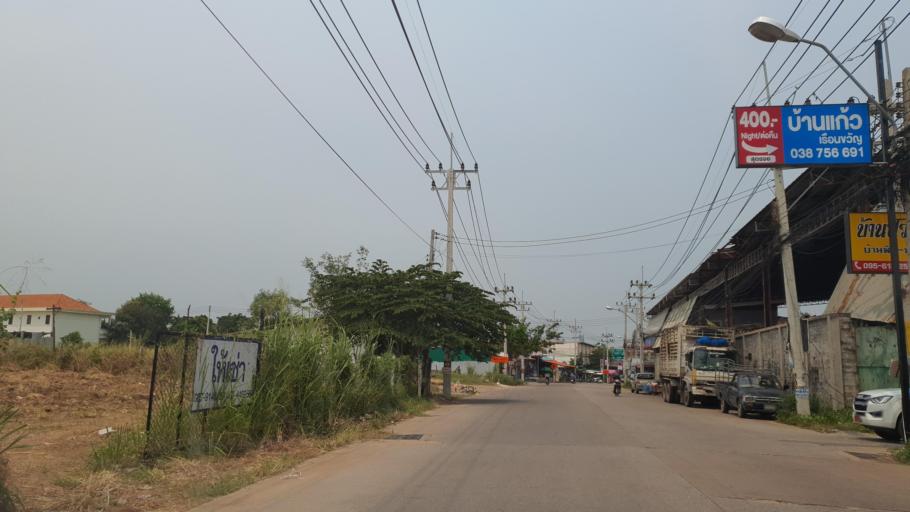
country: TH
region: Chon Buri
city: Phatthaya
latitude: 12.8998
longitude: 100.9027
